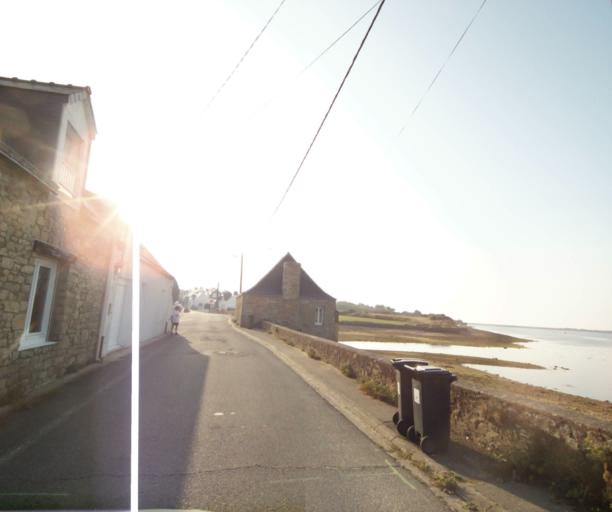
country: FR
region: Brittany
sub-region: Departement du Morbihan
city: Riantec
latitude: 47.7089
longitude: -3.3270
